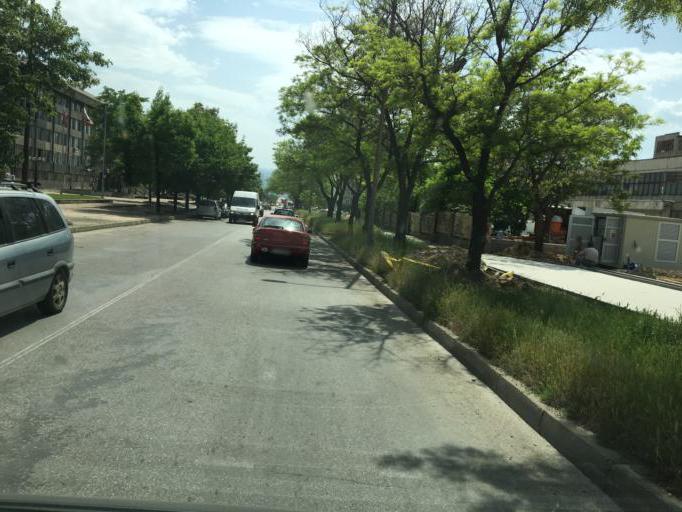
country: BG
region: Blagoevgrad
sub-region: Obshtina Blagoevgrad
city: Blagoevgrad
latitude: 42.0083
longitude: 23.0861
